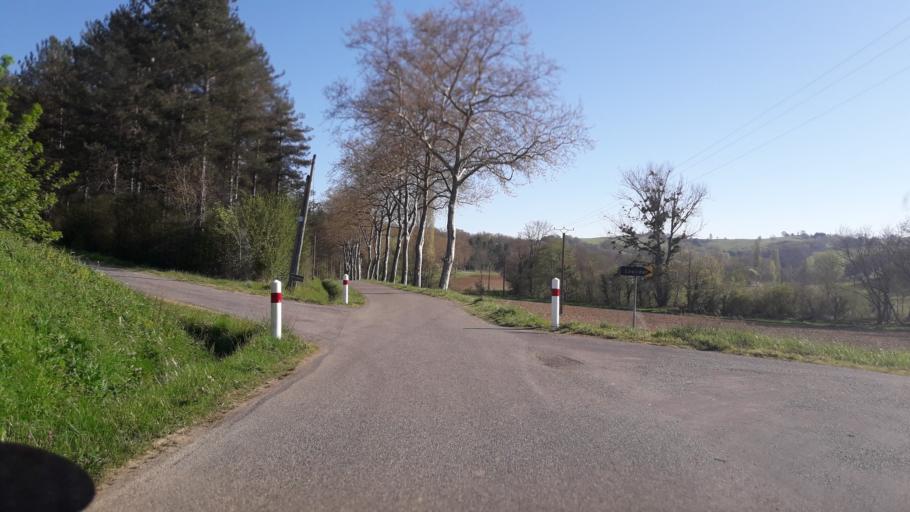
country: FR
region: Midi-Pyrenees
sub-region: Departement de la Haute-Garonne
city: Montesquieu-Volvestre
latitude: 43.1944
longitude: 1.2570
